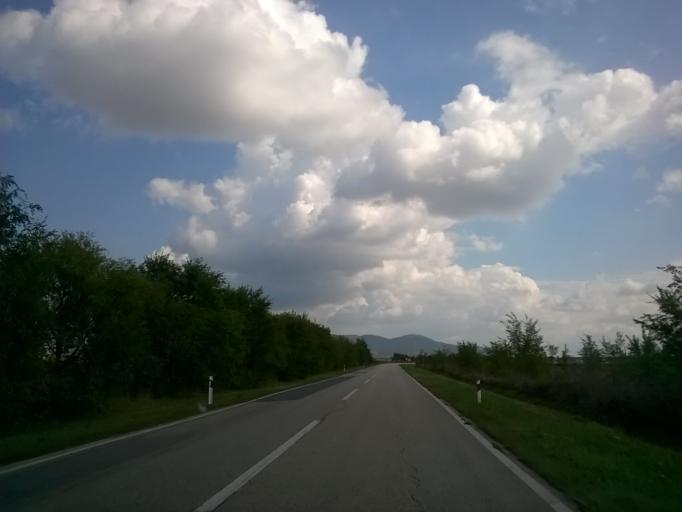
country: RS
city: Pavlis
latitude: 45.1553
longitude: 21.2512
